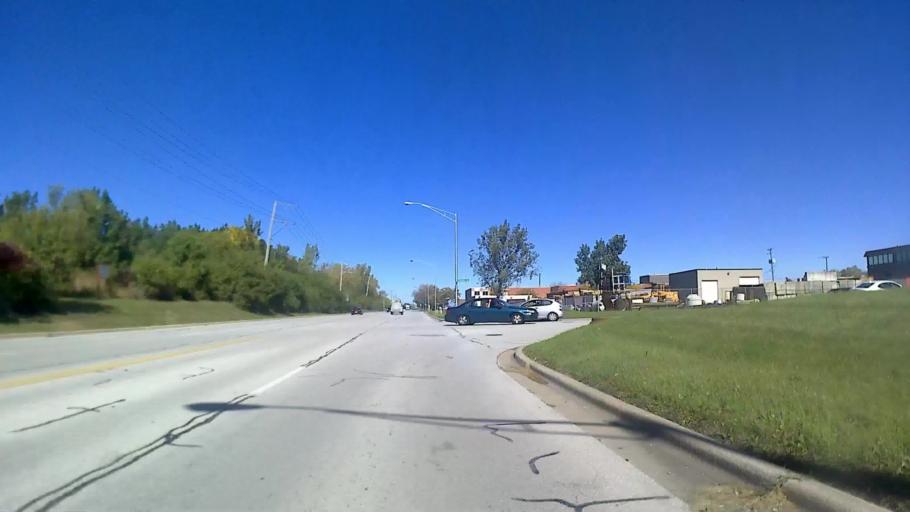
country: US
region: Illinois
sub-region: DuPage County
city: Addison
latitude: 41.9134
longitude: -88.0080
